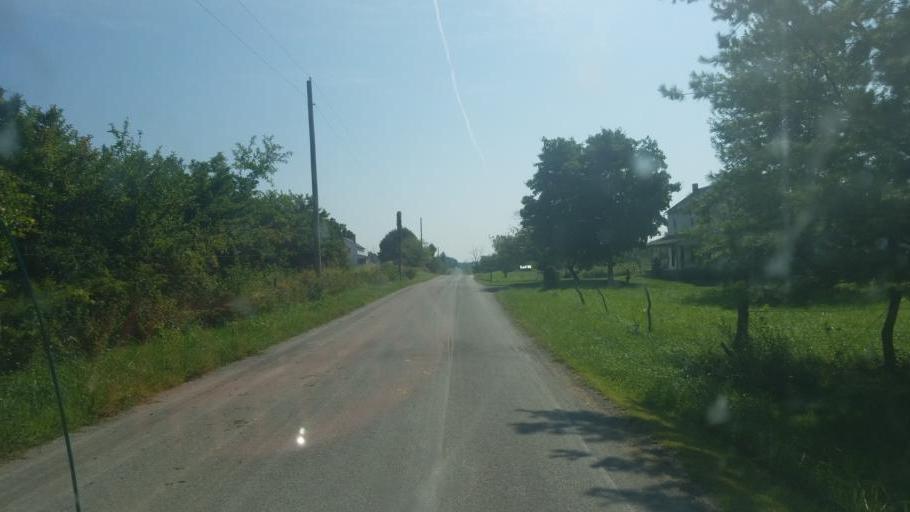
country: US
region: Ohio
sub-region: Wayne County
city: West Salem
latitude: 41.0069
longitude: -82.1518
